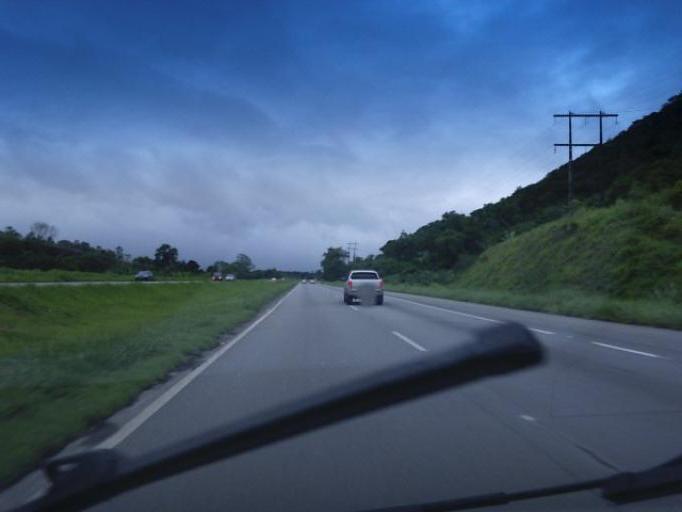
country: BR
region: Sao Paulo
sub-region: Miracatu
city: Miracatu
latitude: -24.3194
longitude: -47.5319
